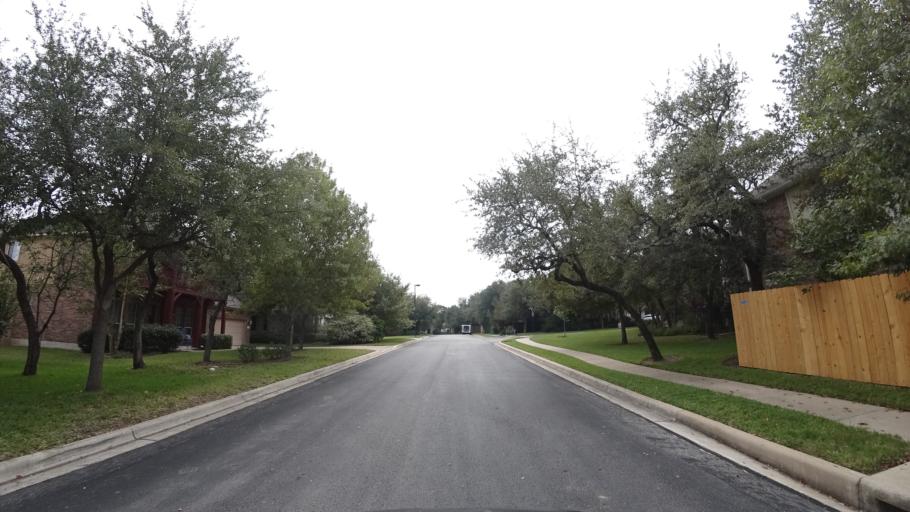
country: US
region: Texas
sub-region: Travis County
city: Shady Hollow
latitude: 30.1886
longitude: -97.9031
